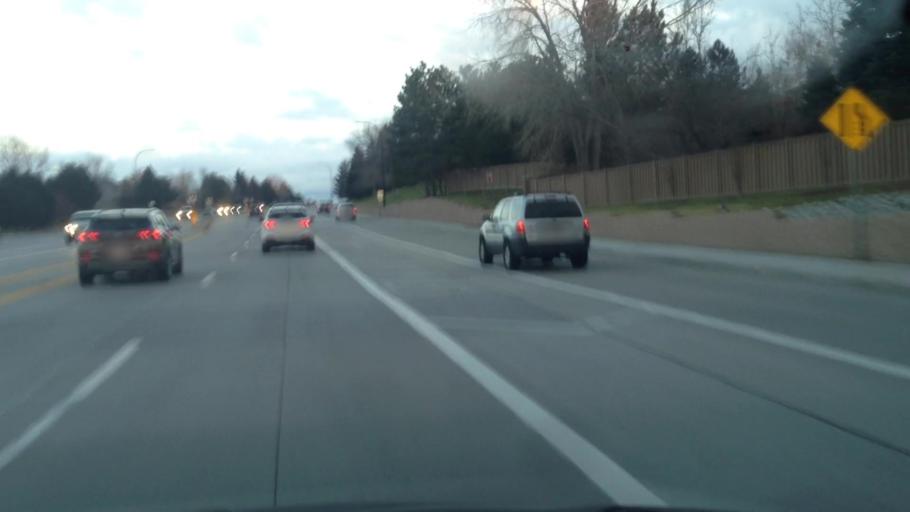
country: US
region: Colorado
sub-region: Douglas County
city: Carriage Club
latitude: 39.5417
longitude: -104.9132
